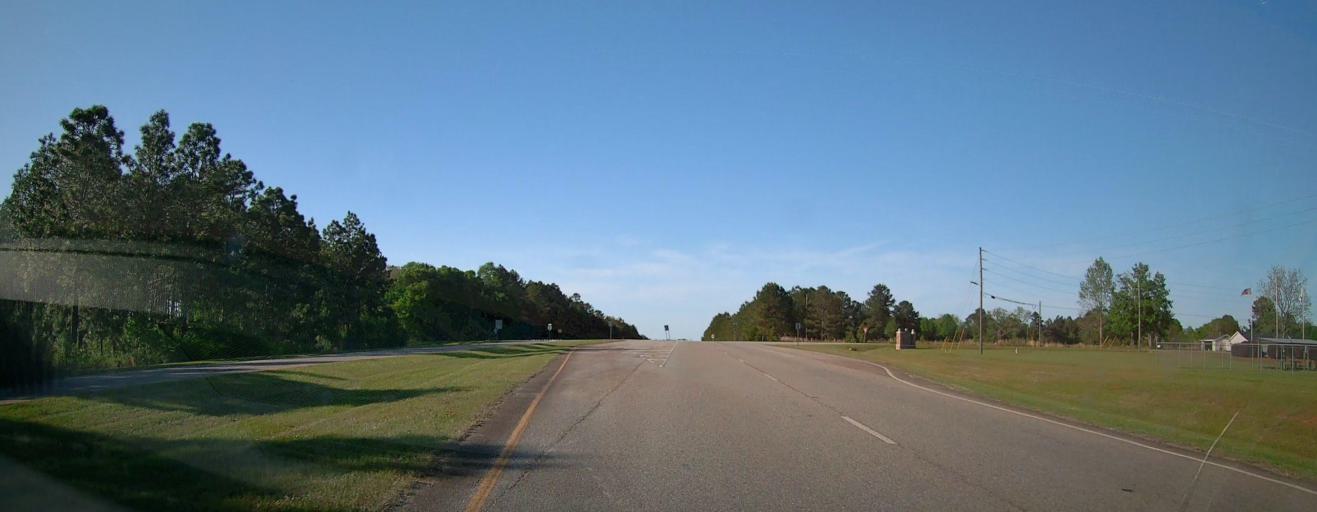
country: US
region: Georgia
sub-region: Houston County
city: Perry
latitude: 32.4657
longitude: -83.7781
